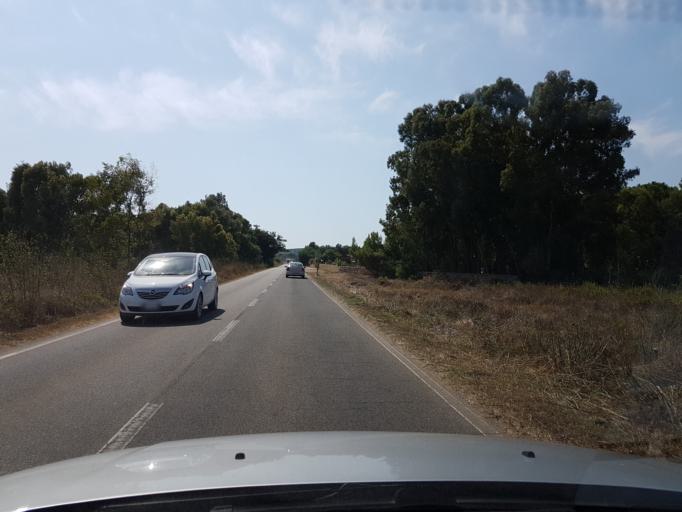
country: IT
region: Sardinia
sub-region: Provincia di Oristano
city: Cabras
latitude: 39.9158
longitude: 8.4588
